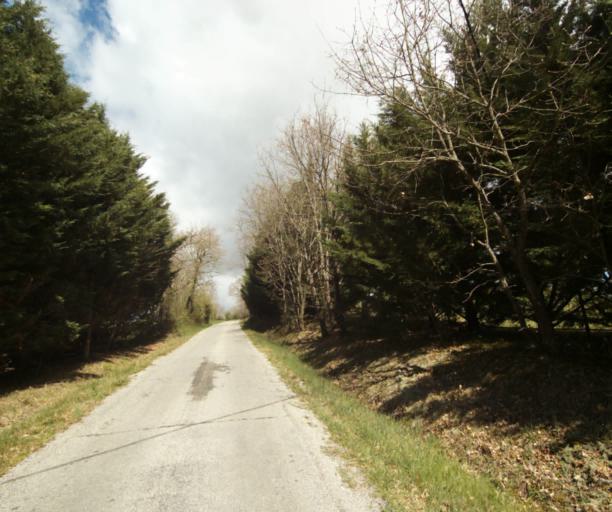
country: FR
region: Midi-Pyrenees
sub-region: Departement de l'Ariege
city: Saverdun
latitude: 43.1798
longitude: 1.5495
